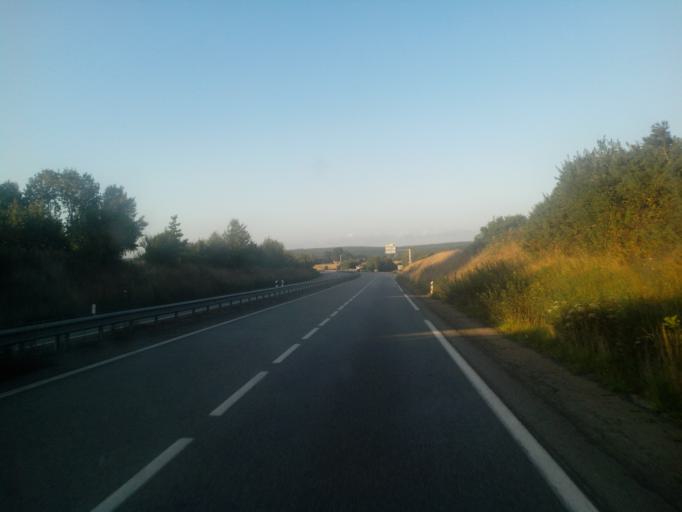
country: FR
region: Brittany
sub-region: Departement des Cotes-d'Armor
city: Loudeac
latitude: 48.1657
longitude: -2.7380
